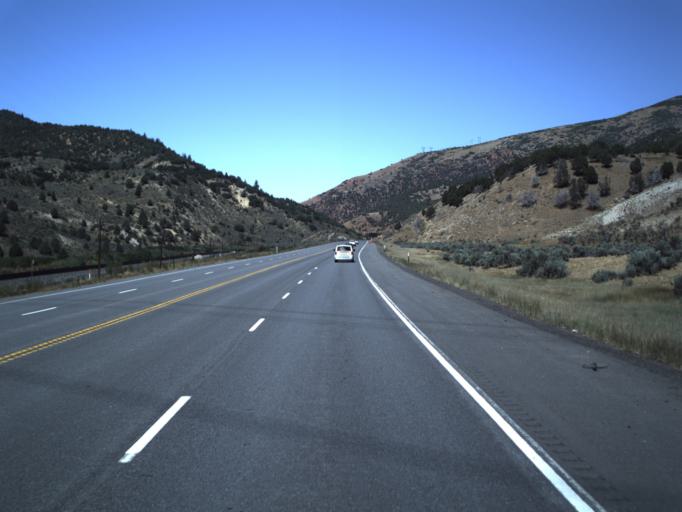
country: US
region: Utah
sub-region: Utah County
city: Mapleton
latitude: 39.9788
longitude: -111.3506
